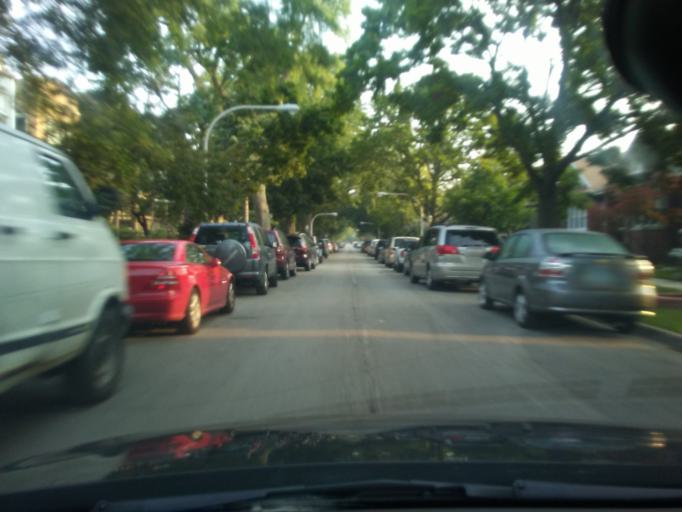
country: US
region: Illinois
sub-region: Cook County
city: Lincolnwood
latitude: 41.9510
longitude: -87.7018
